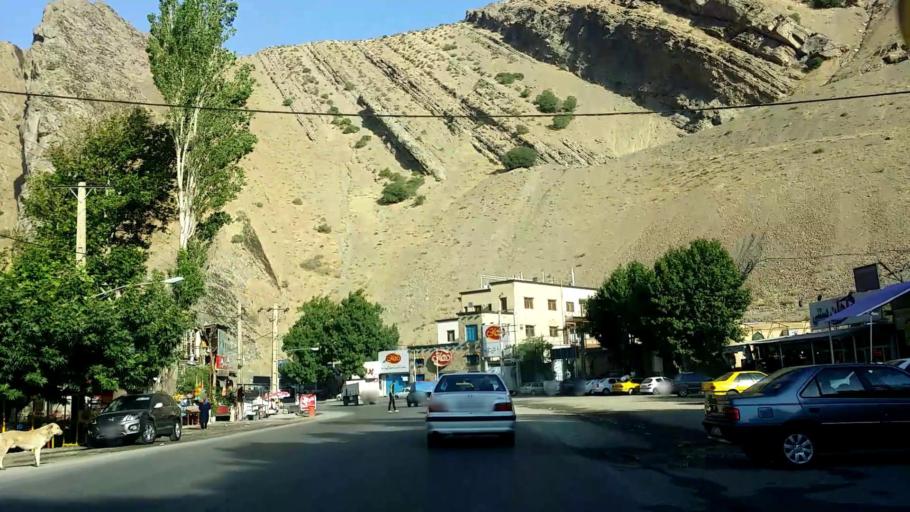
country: IR
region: Tehran
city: Tajrish
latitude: 36.0315
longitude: 51.2308
